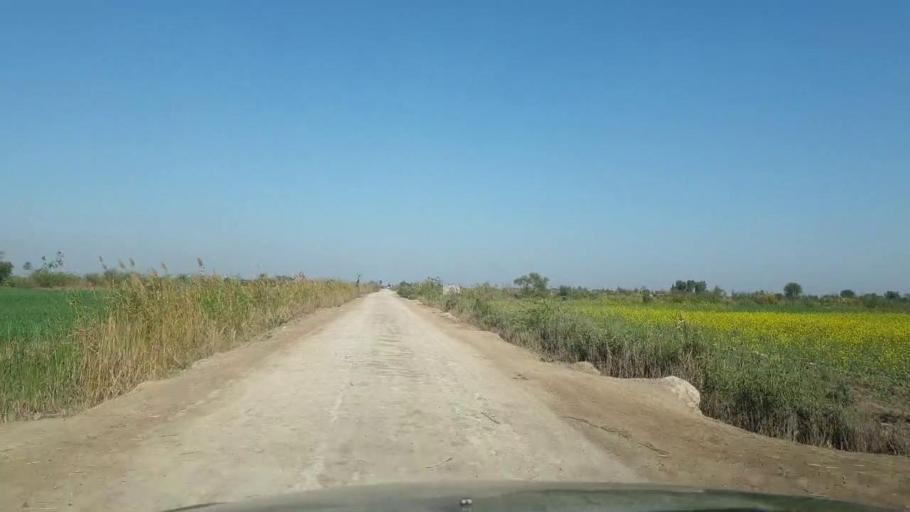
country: PK
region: Sindh
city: Mirpur Khas
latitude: 25.5892
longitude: 69.0557
